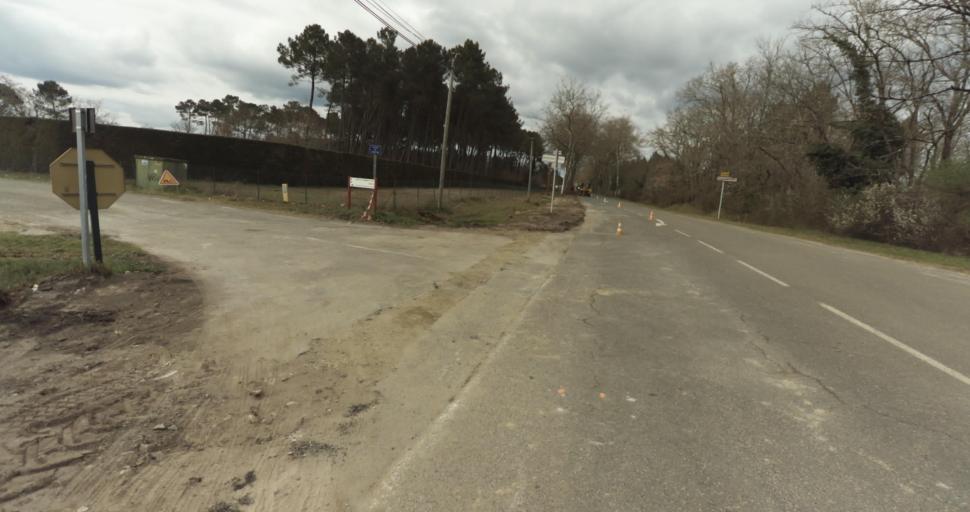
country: FR
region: Aquitaine
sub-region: Departement des Landes
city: Roquefort
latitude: 44.0469
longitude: -0.3210
